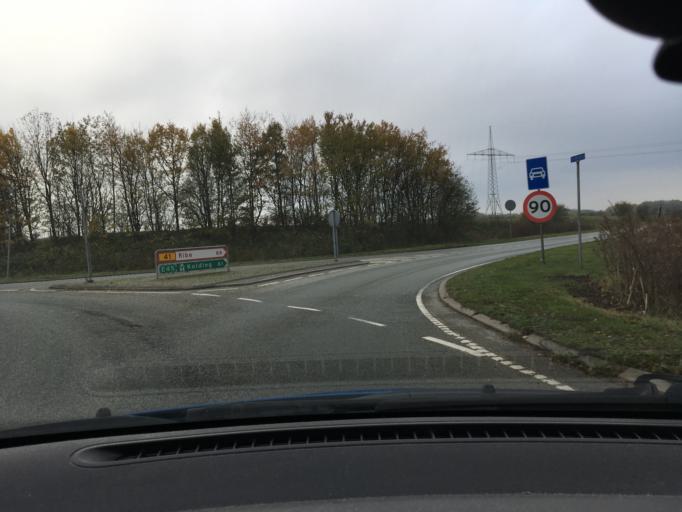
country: DK
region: South Denmark
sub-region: Aabenraa Kommune
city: Aabenraa
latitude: 55.0027
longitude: 9.4178
